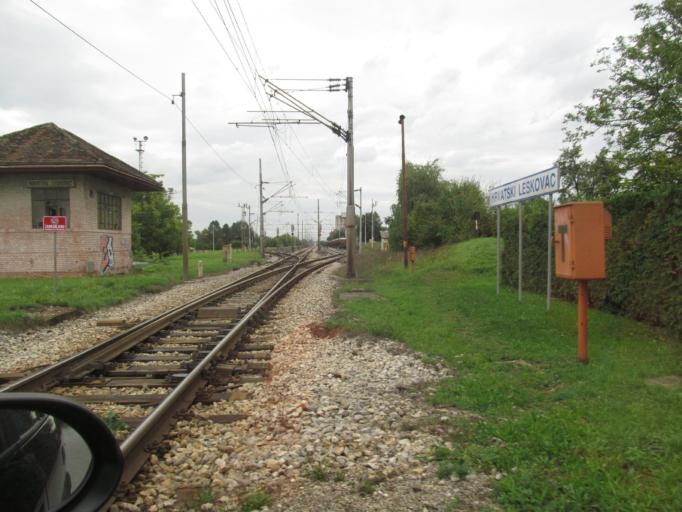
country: HR
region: Grad Zagreb
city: Brezovica
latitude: 45.7434
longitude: 15.8892
